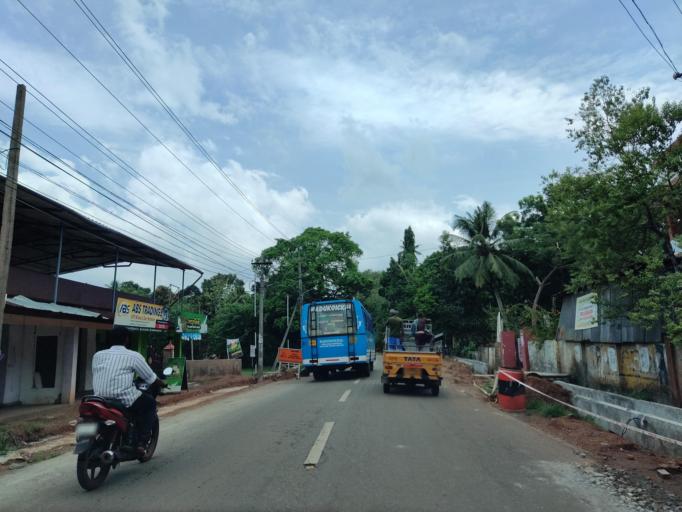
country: IN
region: Kerala
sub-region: Alappuzha
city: Mavelikara
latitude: 9.2267
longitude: 76.6229
